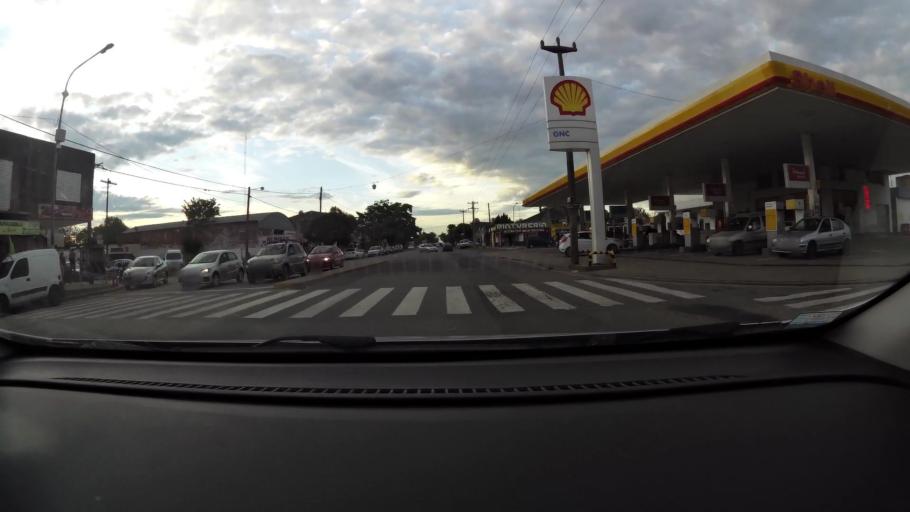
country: AR
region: Buenos Aires
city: San Nicolas de los Arroyos
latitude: -33.3276
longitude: -60.2347
